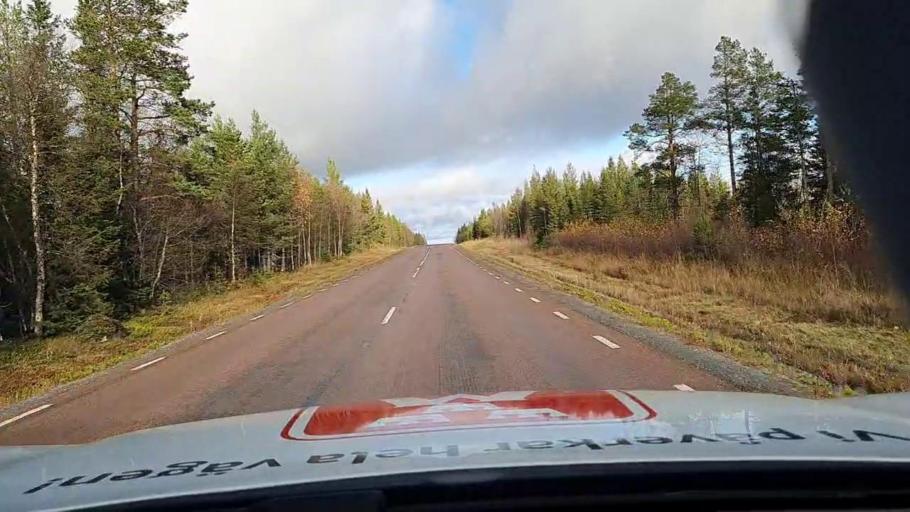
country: SE
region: Jaemtland
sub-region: Krokoms Kommun
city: Valla
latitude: 63.1280
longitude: 13.9325
